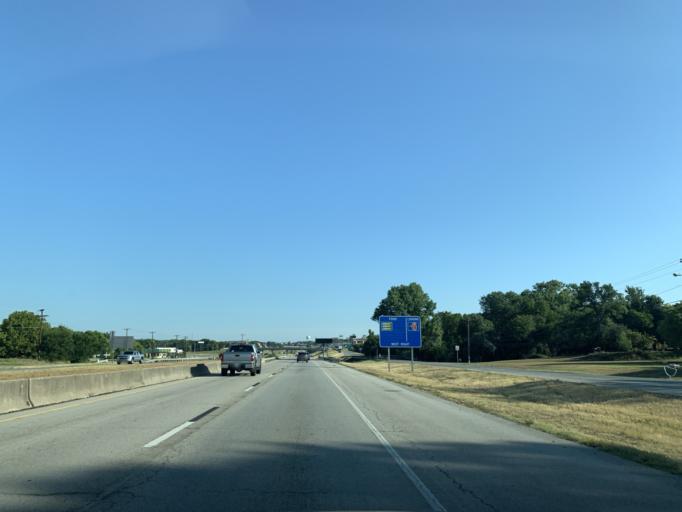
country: US
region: Texas
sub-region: Tarrant County
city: Azle
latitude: 32.8857
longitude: -97.5382
